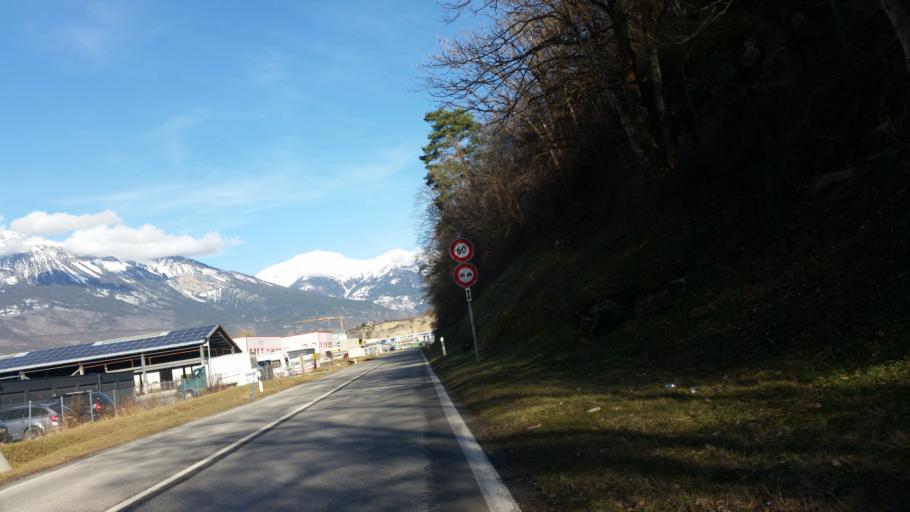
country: CH
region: Valais
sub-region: Sierre District
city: Chalais
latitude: 46.2734
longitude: 7.5240
